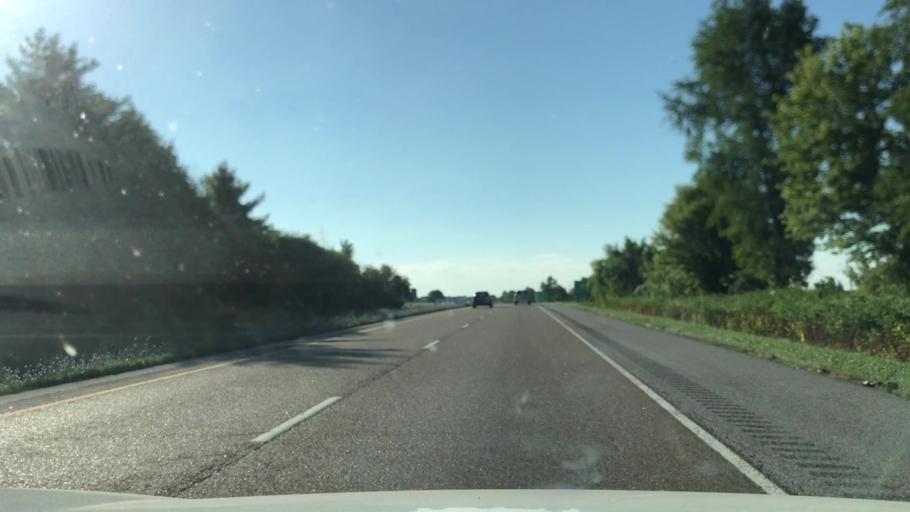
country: US
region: Illinois
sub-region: Saint Clair County
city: Scott Air Force Base
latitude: 38.5568
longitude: -89.8225
